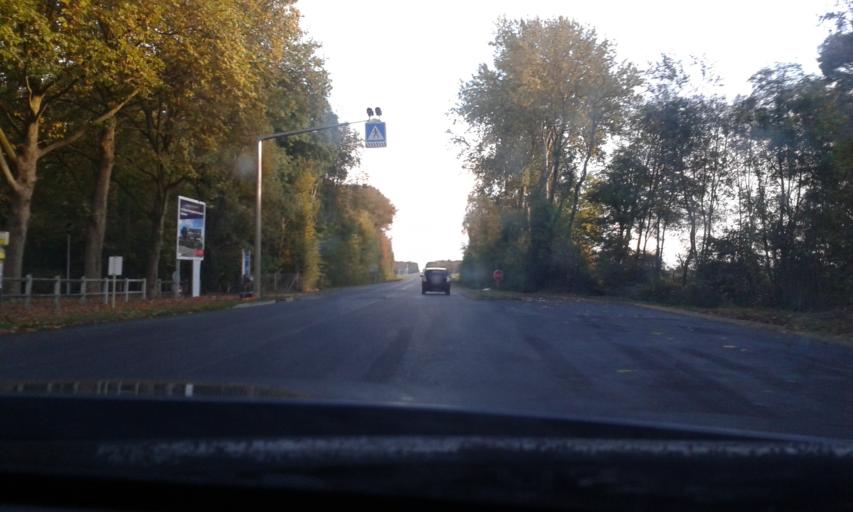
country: FR
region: Centre
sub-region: Departement d'Eure-et-Loir
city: Sours
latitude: 48.4033
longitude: 1.5507
